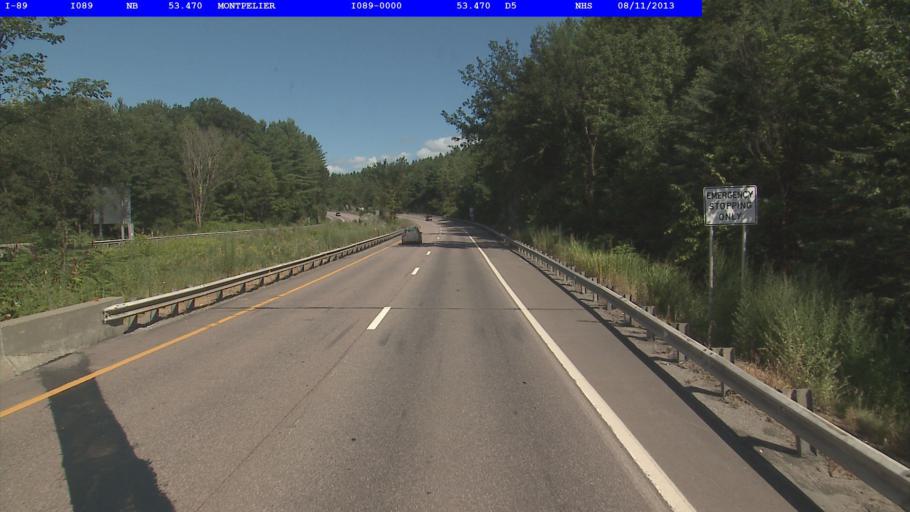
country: US
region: Vermont
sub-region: Washington County
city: Montpelier
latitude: 44.2577
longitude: -72.6009
